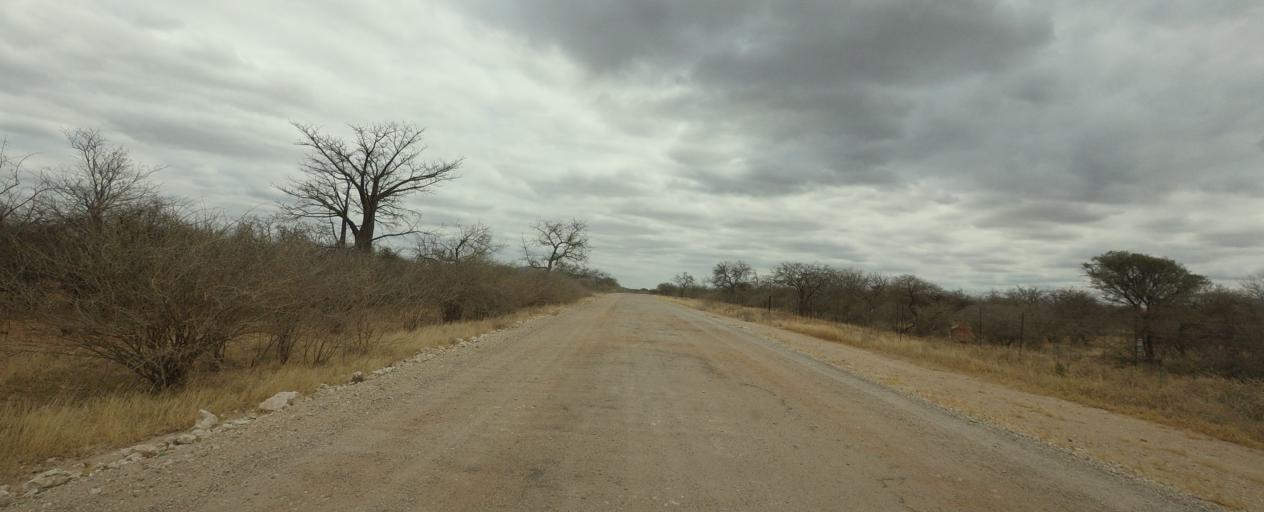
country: BW
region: Central
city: Mogapi
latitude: -22.7811
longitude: 28.3179
